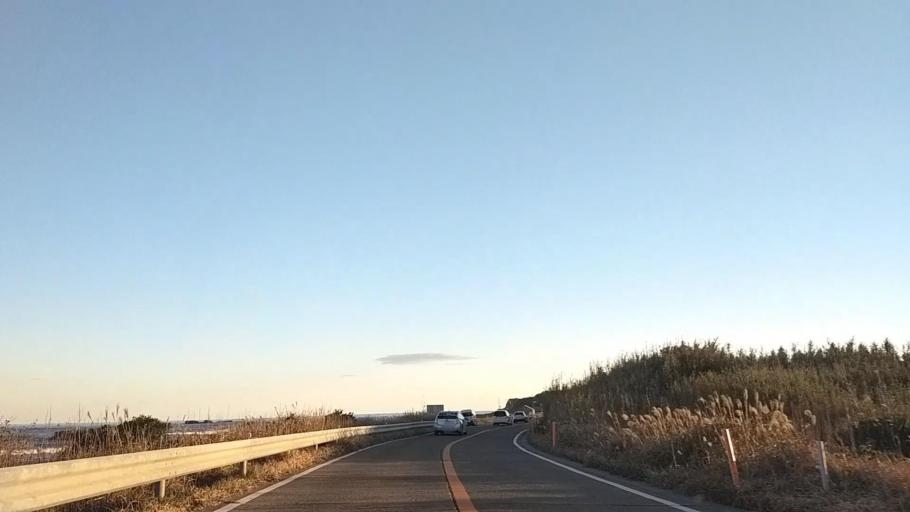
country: JP
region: Chiba
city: Hasaki
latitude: 35.7268
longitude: 140.8676
